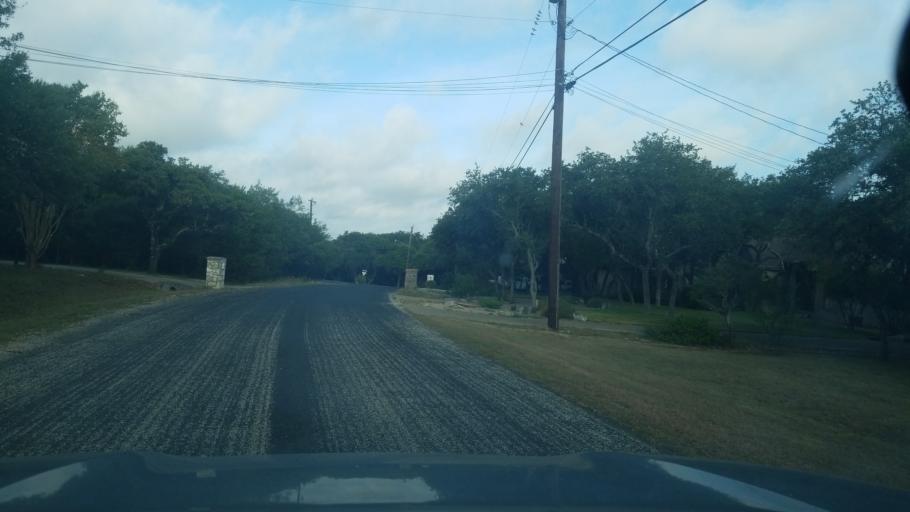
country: US
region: Texas
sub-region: Bexar County
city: Timberwood Park
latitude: 29.7021
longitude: -98.5035
